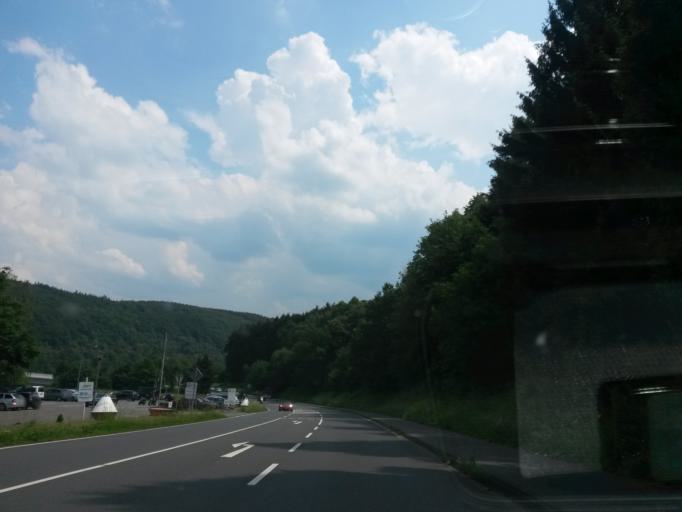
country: DE
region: North Rhine-Westphalia
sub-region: Regierungsbezirk Arnsberg
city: Olpe
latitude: 51.0760
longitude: 7.8543
